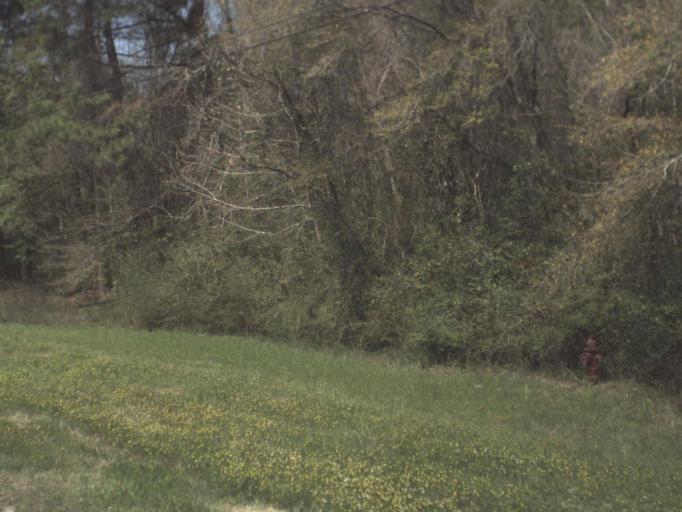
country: US
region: Florida
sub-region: Gadsden County
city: Quincy
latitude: 30.5603
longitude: -84.5362
